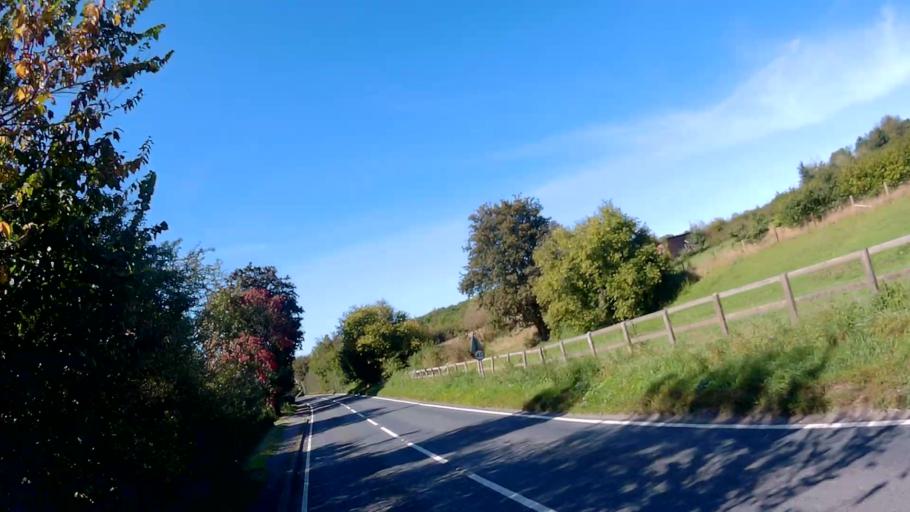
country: GB
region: England
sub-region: Hampshire
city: Overton
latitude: 51.2340
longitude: -1.3117
